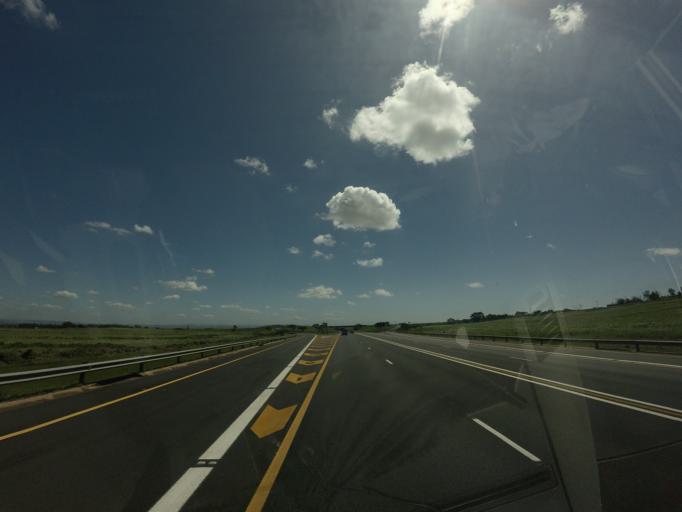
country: ZA
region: KwaZulu-Natal
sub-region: iLembe District Municipality
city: Mandeni
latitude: -29.1271
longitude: 31.5616
